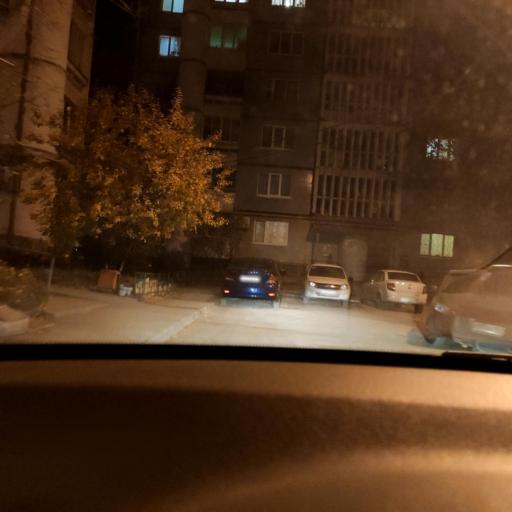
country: RU
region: Samara
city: Samara
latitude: 53.2502
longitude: 50.2113
